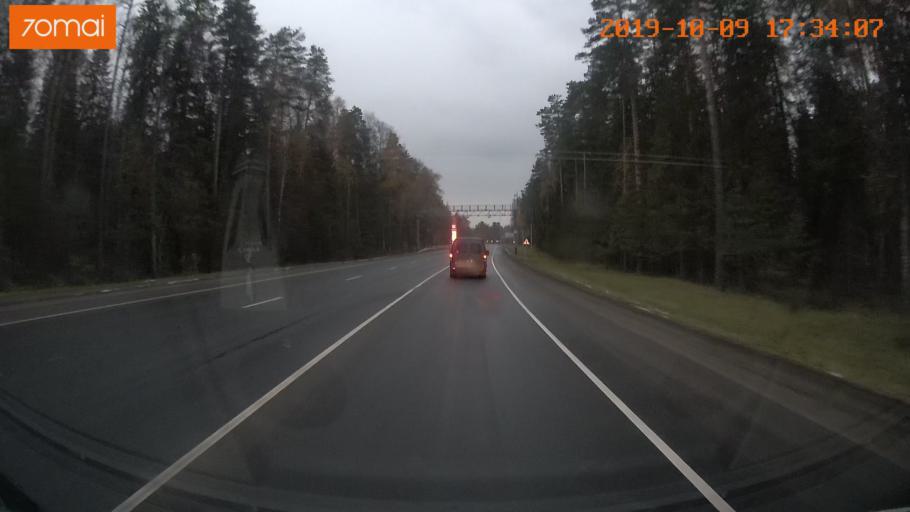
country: RU
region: Ivanovo
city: Bogorodskoye
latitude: 57.1096
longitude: 41.0150
